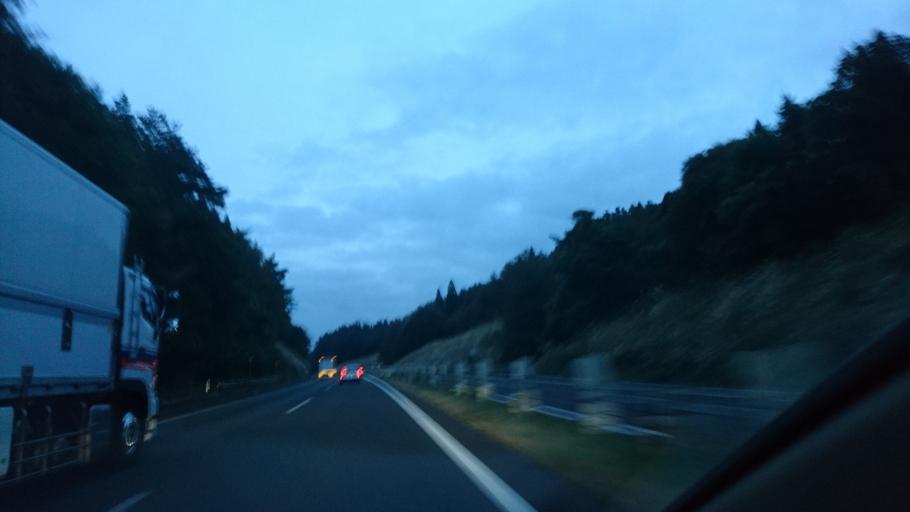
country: JP
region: Iwate
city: Hanamaki
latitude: 39.5352
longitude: 141.1033
